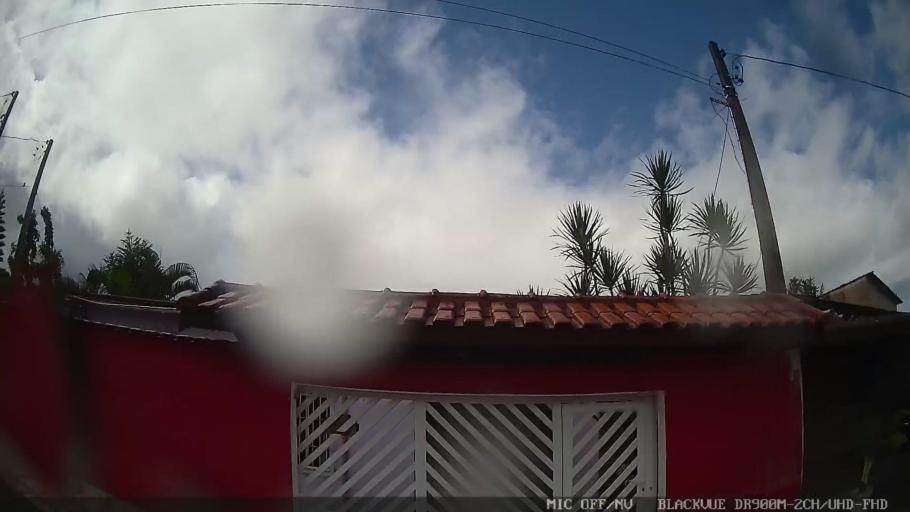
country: BR
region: Sao Paulo
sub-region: Itanhaem
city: Itanhaem
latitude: -24.2352
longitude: -46.8996
